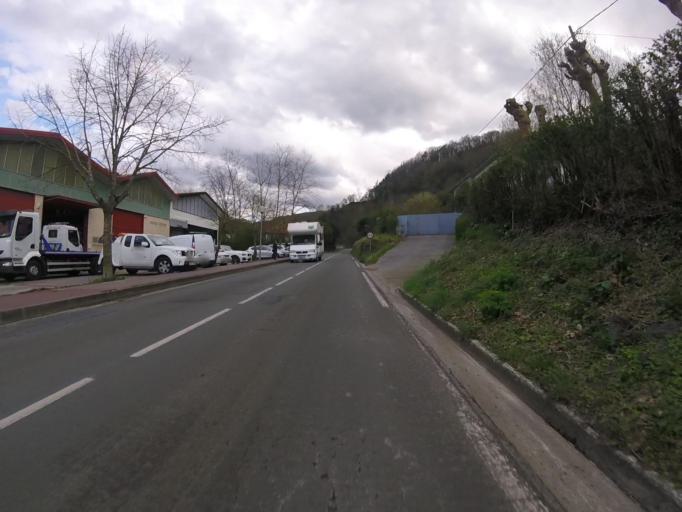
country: ES
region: Basque Country
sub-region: Provincia de Guipuzcoa
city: Errenteria
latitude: 43.2904
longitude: -1.8565
